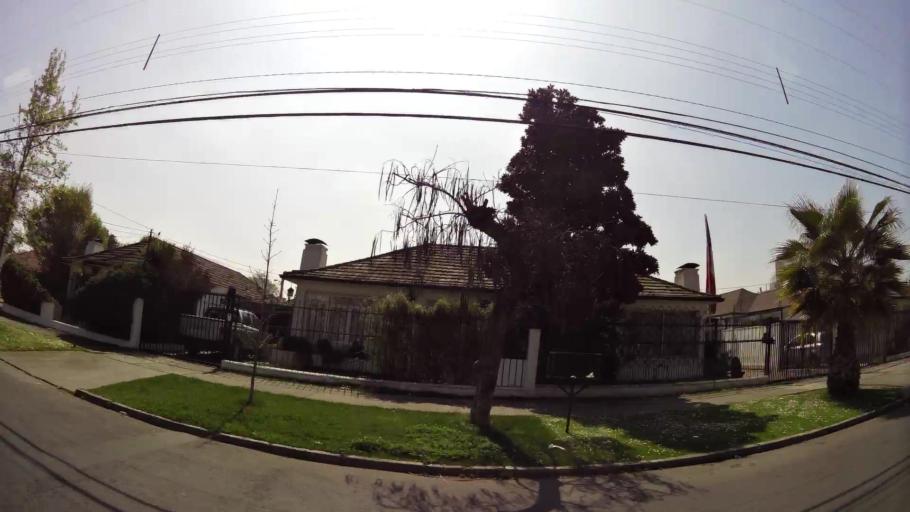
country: CL
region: Santiago Metropolitan
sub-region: Provincia de Santiago
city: Villa Presidente Frei, Nunoa, Santiago, Chile
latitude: -33.4604
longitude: -70.6077
